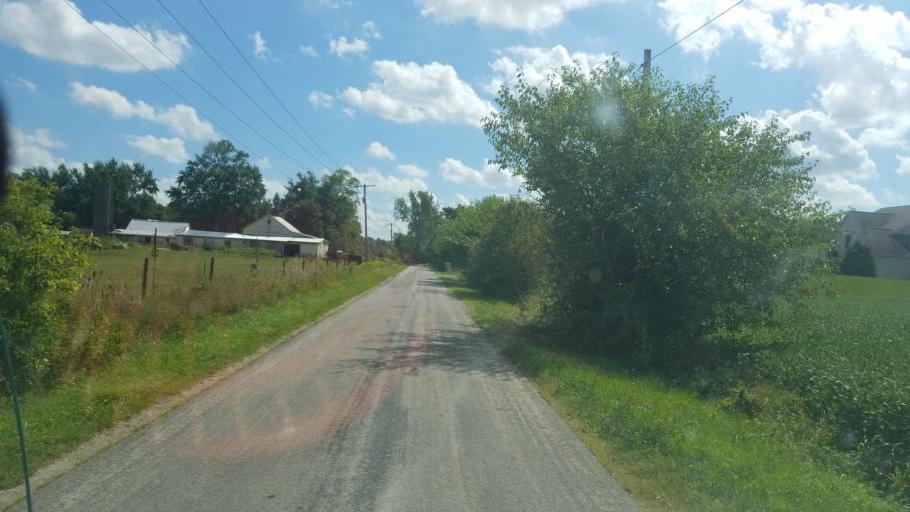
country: US
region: Ohio
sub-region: Union County
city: Richwood
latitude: 40.3433
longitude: -83.2439
